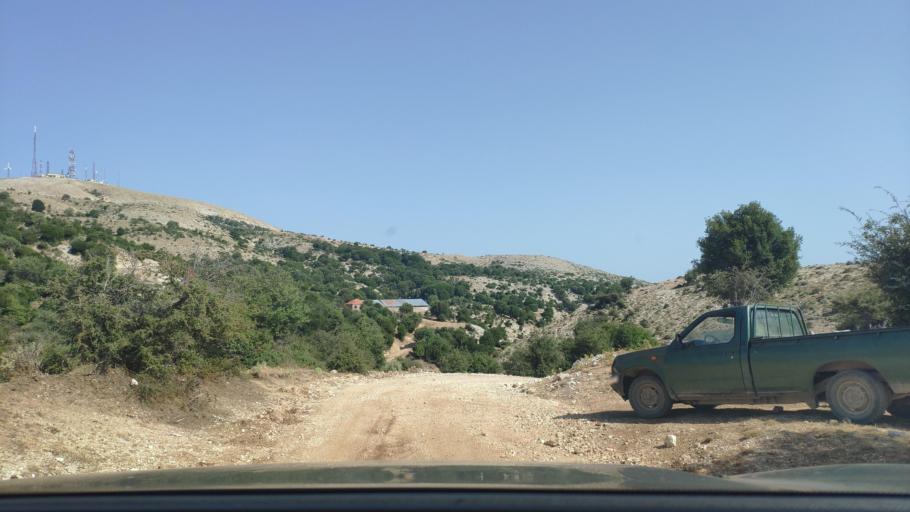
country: GR
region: West Greece
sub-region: Nomos Aitolias kai Akarnanias
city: Monastirakion
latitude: 38.7997
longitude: 20.9972
